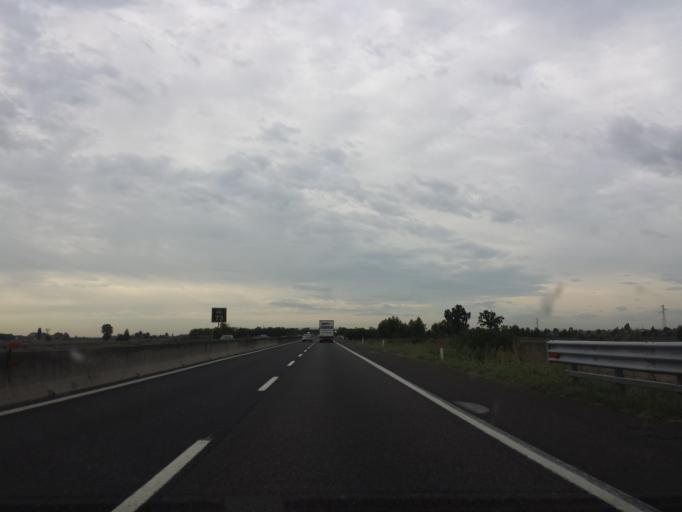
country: IT
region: Veneto
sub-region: Provincia di Padova
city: Pozzonovo
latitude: 45.1971
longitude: 11.7749
